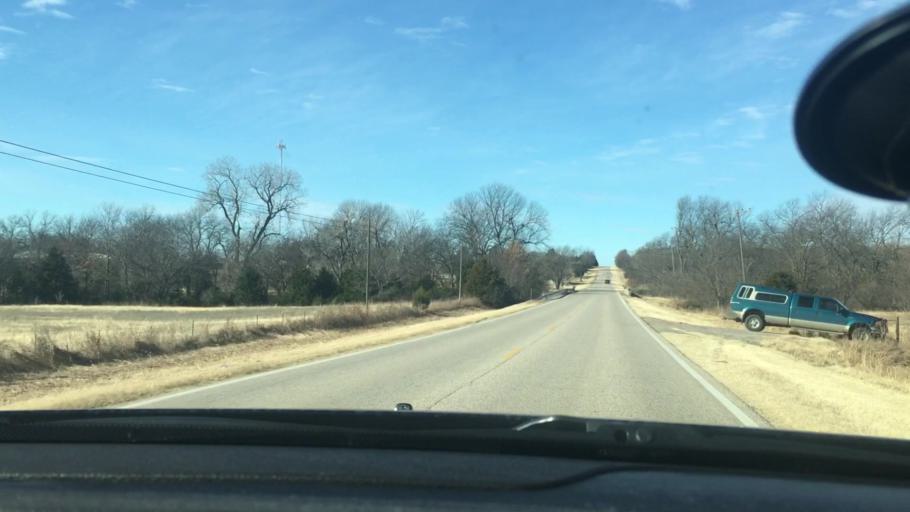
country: US
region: Oklahoma
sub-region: Garvin County
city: Stratford
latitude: 34.9860
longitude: -96.9642
